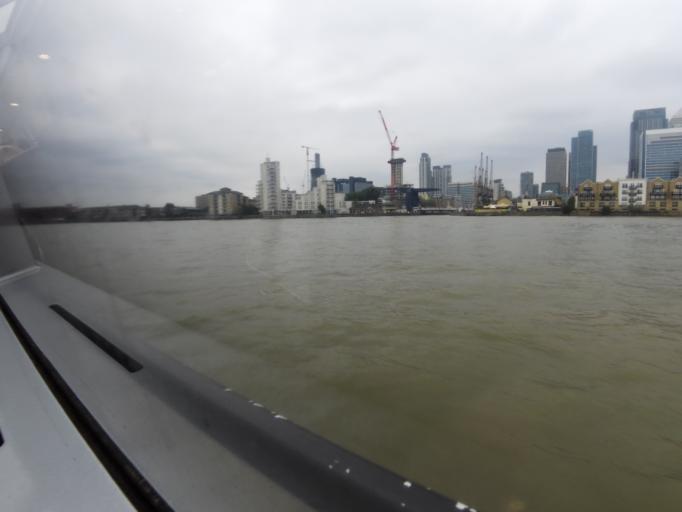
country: GB
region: England
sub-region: Greater London
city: Poplar
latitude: 51.5018
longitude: -0.0050
